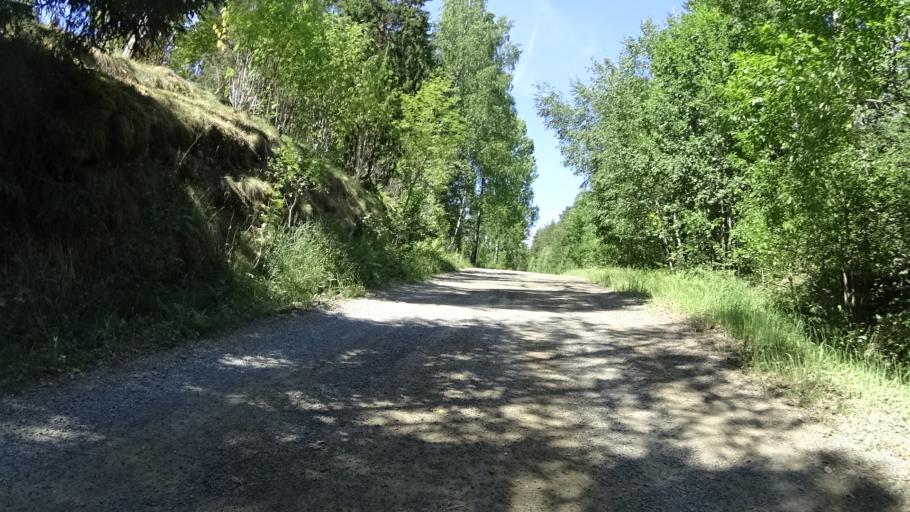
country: FI
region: Uusimaa
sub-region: Raaseporin
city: Pohja
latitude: 60.0952
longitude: 23.5645
